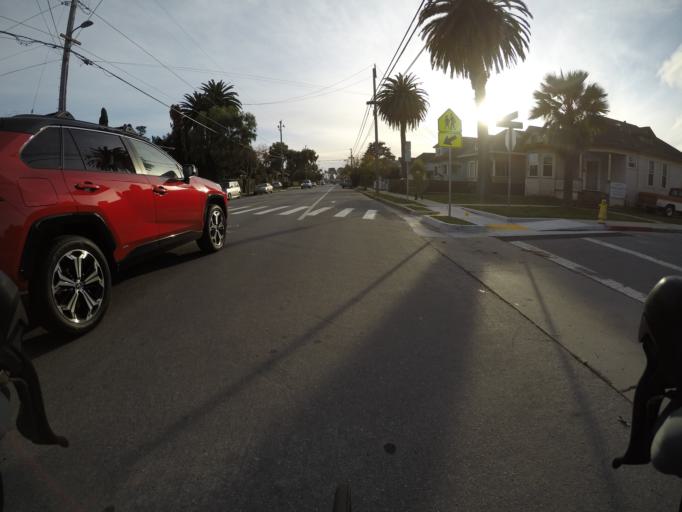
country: US
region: California
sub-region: Santa Cruz County
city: Santa Cruz
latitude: 36.9802
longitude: -122.0146
